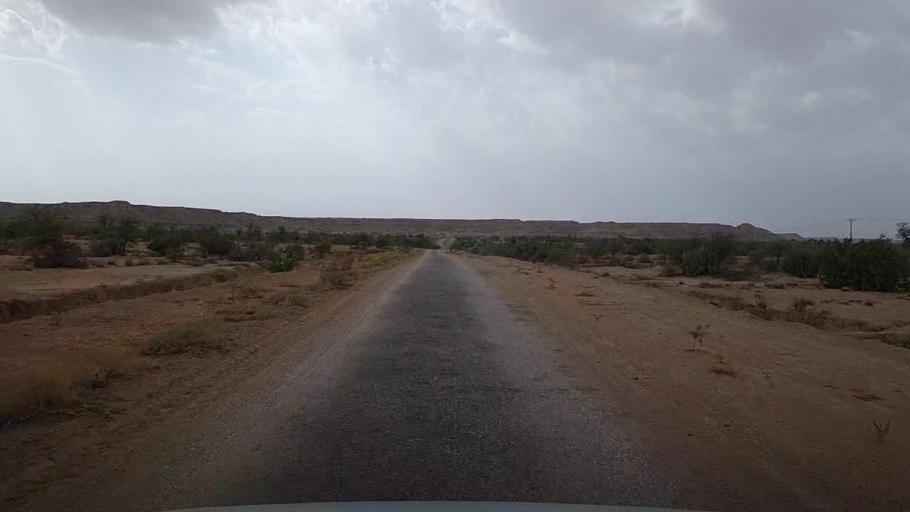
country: PK
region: Sindh
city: Jamshoro
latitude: 25.4133
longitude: 67.6994
